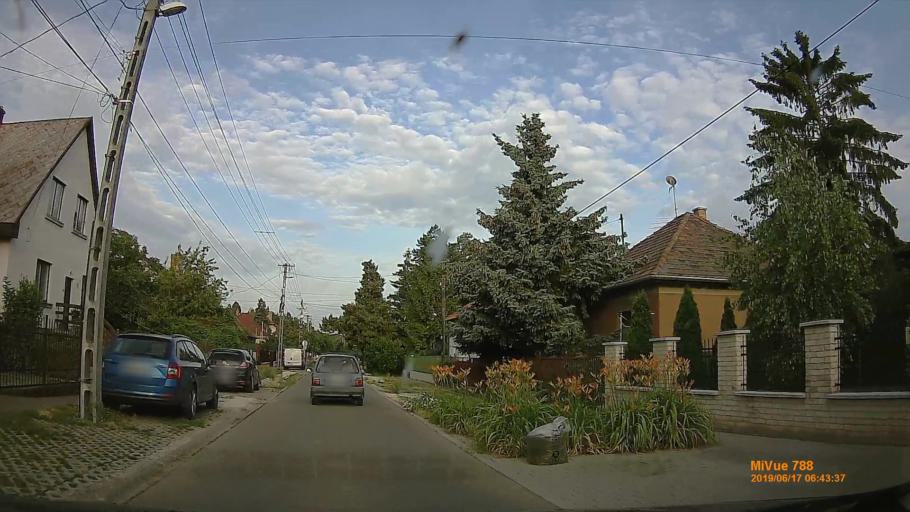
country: HU
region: Budapest
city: Budapest XVI. keruelet
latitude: 47.5068
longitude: 19.1748
